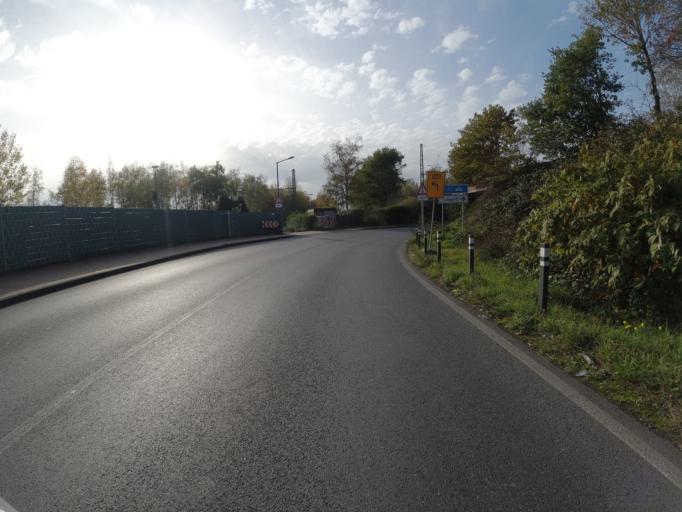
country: DE
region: North Rhine-Westphalia
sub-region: Regierungsbezirk Dusseldorf
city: Hochfeld
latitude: 51.3863
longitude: 6.6900
